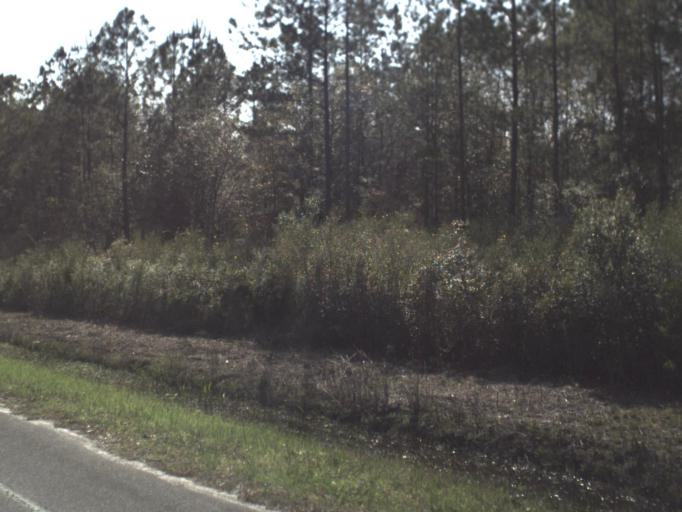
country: US
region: Florida
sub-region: Wakulla County
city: Crawfordville
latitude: 30.0448
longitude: -84.4947
